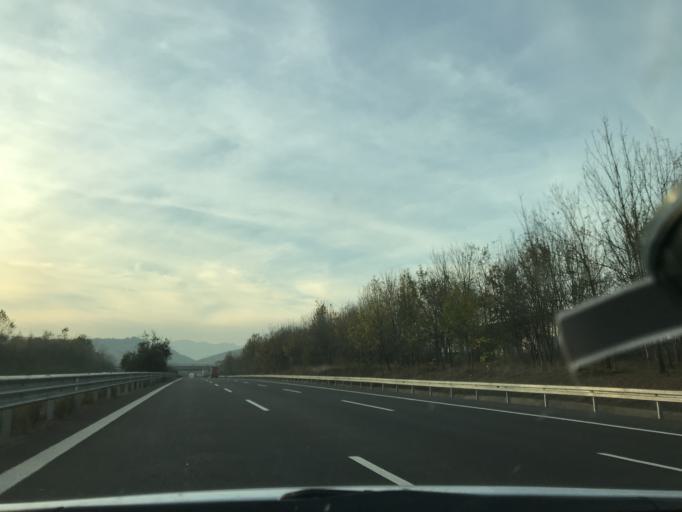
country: TR
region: Duzce
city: Gumusova
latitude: 40.8406
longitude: 30.9830
